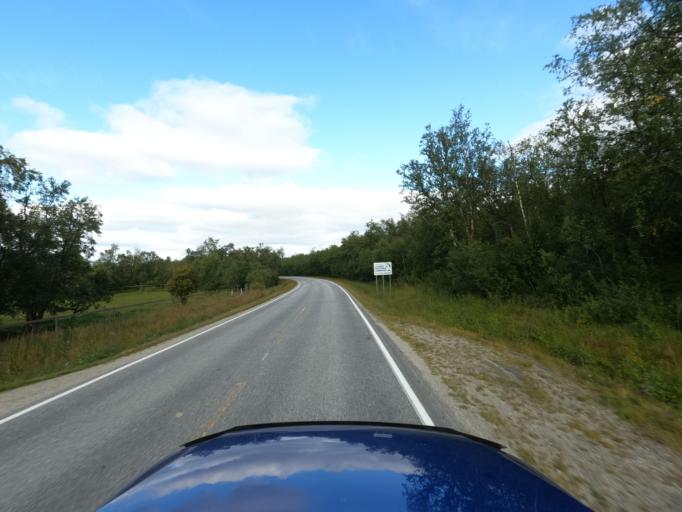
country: NO
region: Finnmark Fylke
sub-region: Porsanger
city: Lakselv
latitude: 70.0255
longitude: 24.9707
